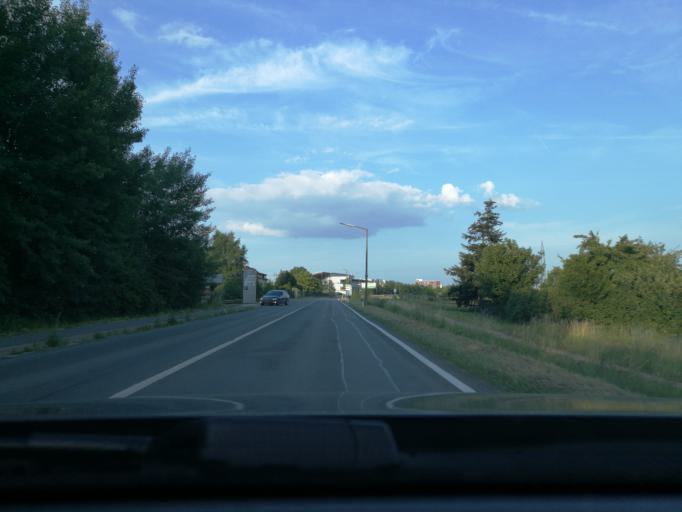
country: DE
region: Bavaria
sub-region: Regierungsbezirk Mittelfranken
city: Erlangen
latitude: 49.5530
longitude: 10.9992
